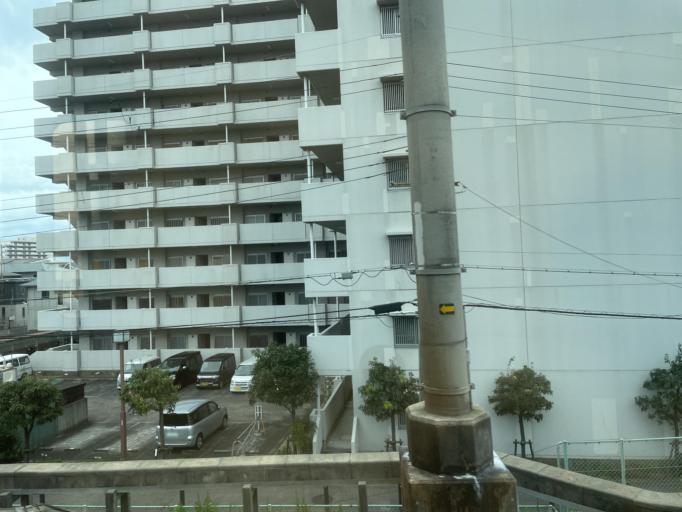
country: JP
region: Hyogo
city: Nishinomiya-hama
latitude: 34.7445
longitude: 135.3475
